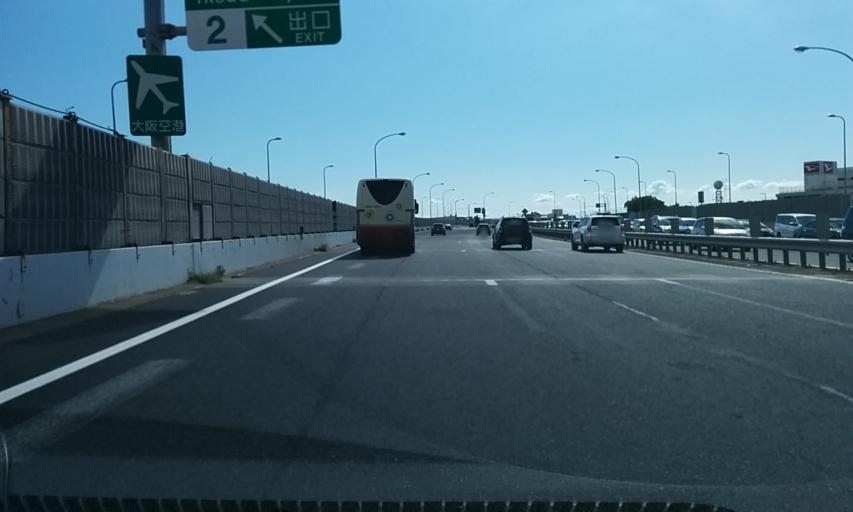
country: JP
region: Osaka
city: Ikeda
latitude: 34.8083
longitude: 135.4289
